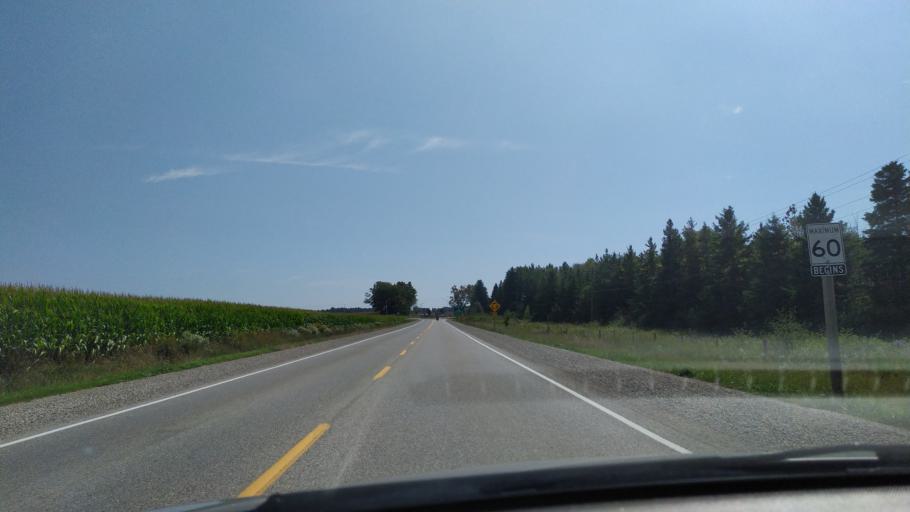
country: CA
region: Ontario
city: Ingersoll
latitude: 43.1004
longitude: -80.8740
